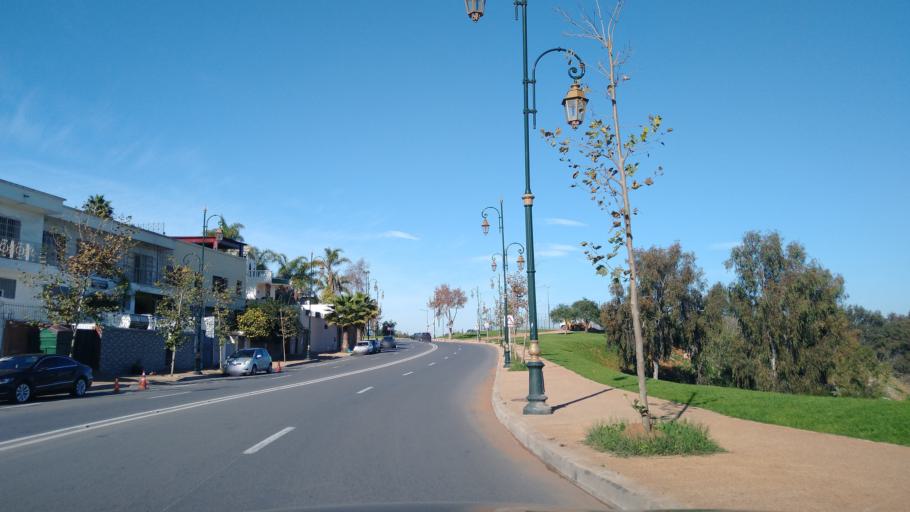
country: MA
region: Rabat-Sale-Zemmour-Zaer
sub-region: Rabat
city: Rabat
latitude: 33.9980
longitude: -6.8245
